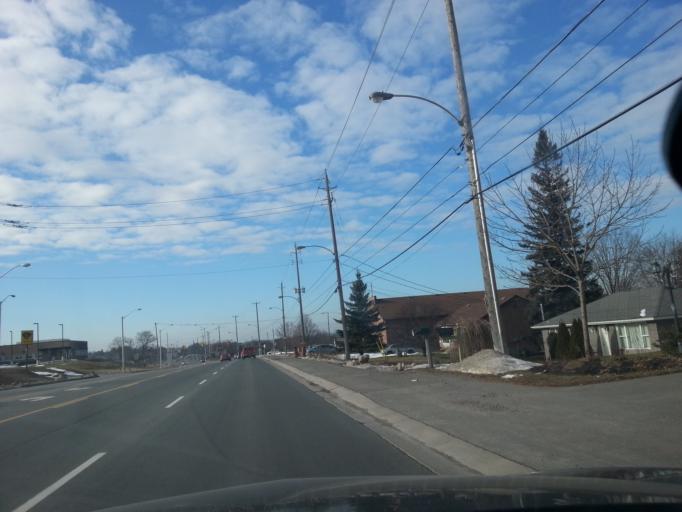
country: CA
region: Ontario
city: Peterborough
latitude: 44.2932
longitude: -78.2862
